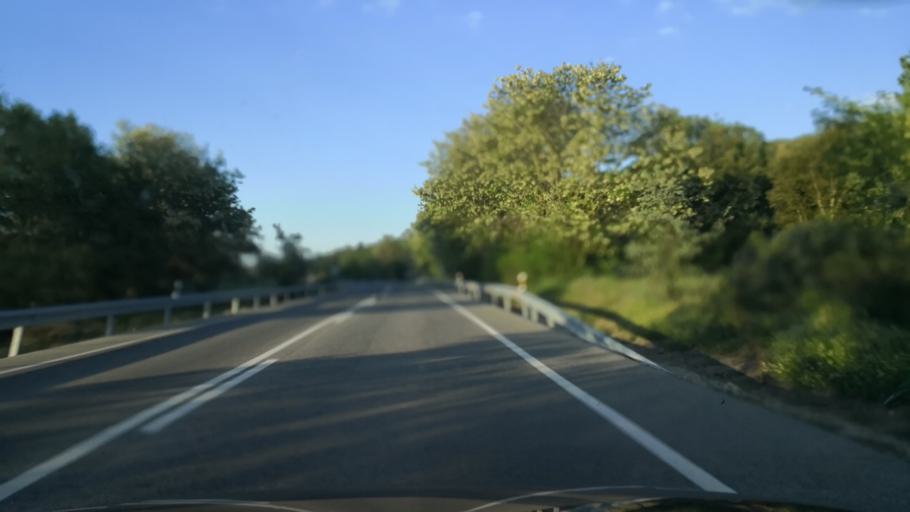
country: ES
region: Extremadura
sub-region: Provincia de Caceres
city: Valencia de Alcantara
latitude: 39.3680
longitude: -7.2681
